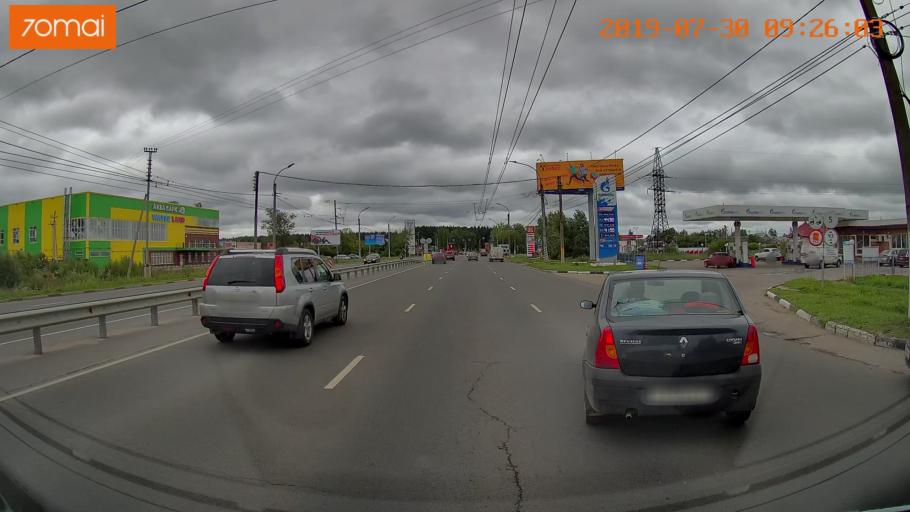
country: RU
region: Ivanovo
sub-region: Gorod Ivanovo
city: Ivanovo
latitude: 56.9484
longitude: 40.9754
